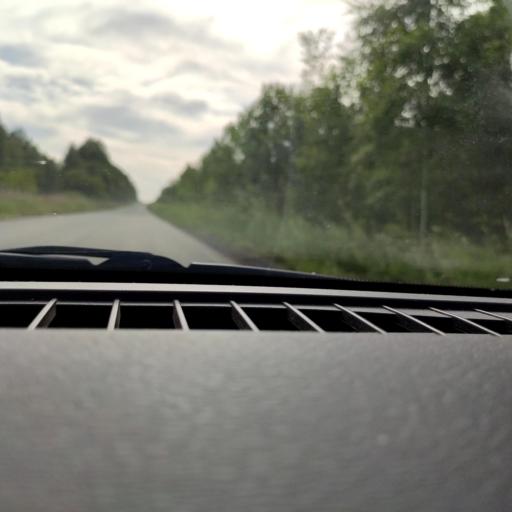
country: RU
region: Perm
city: Polazna
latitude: 58.3365
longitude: 56.1670
